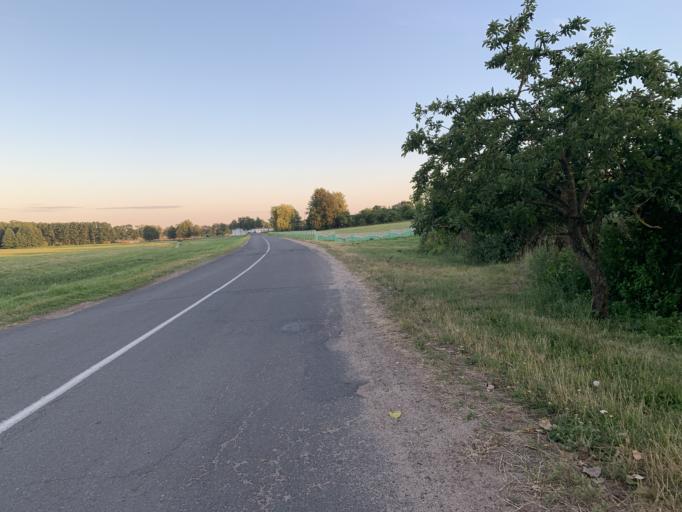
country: BY
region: Minsk
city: Nyasvizh
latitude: 53.2283
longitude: 26.6836
